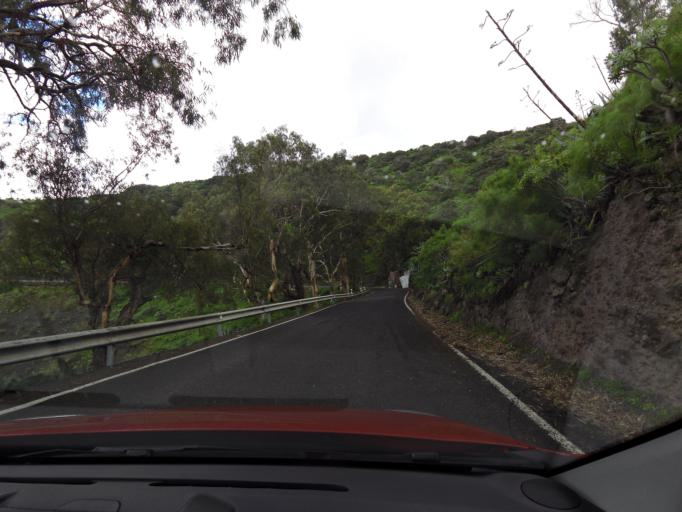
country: ES
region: Canary Islands
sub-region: Provincia de Las Palmas
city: Santa Brigida
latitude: 28.0206
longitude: -15.4658
